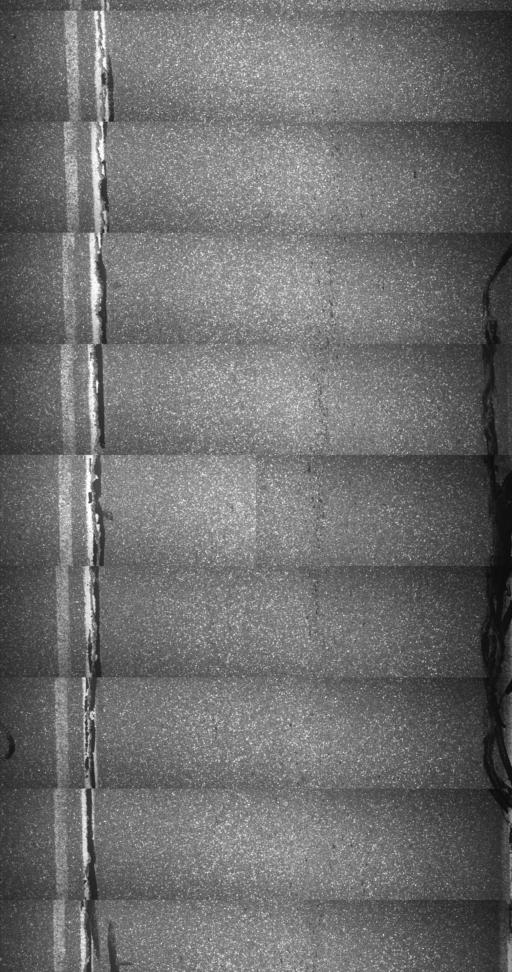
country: US
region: Vermont
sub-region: Orange County
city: Williamstown
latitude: 44.0982
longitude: -72.4458
